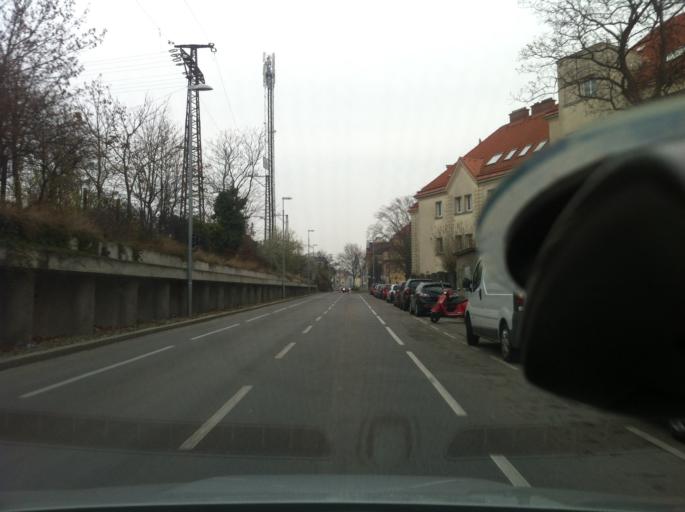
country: AT
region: Lower Austria
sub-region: Politischer Bezirk Modling
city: Perchtoldsdorf
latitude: 48.1923
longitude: 16.2937
